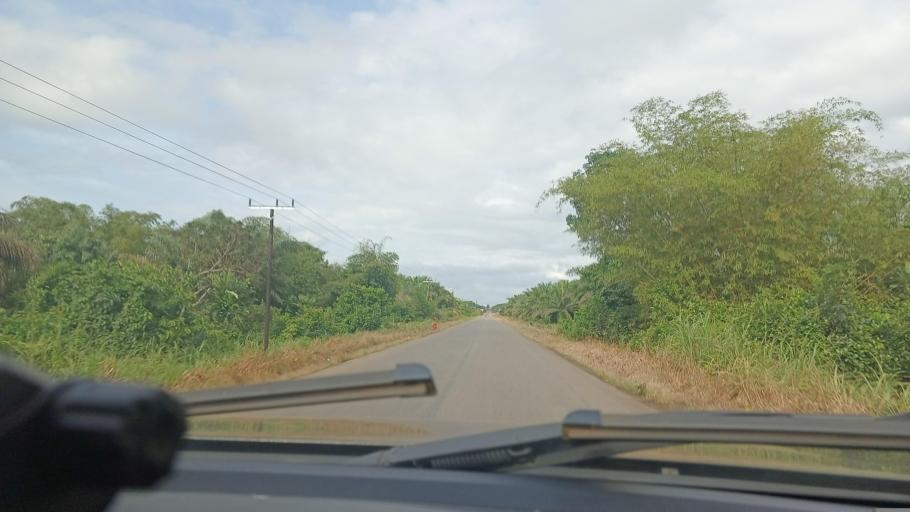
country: LR
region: Bomi
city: Tubmanburg
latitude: 6.7121
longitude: -10.9557
